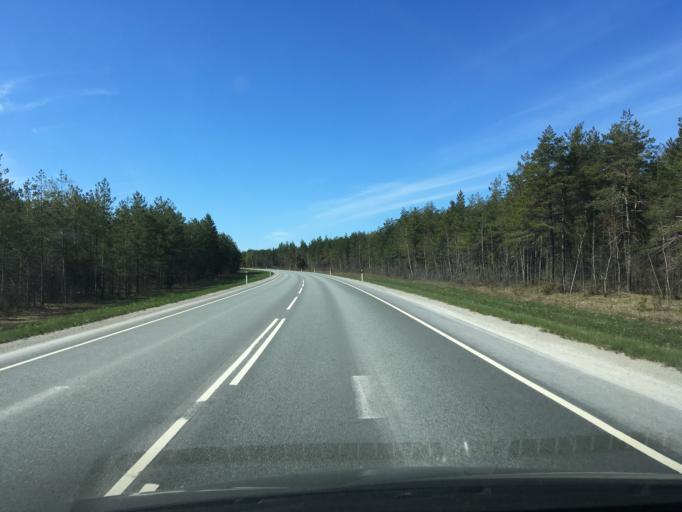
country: EE
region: Laeaene
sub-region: Lihula vald
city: Lihula
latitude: 58.6080
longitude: 23.5637
